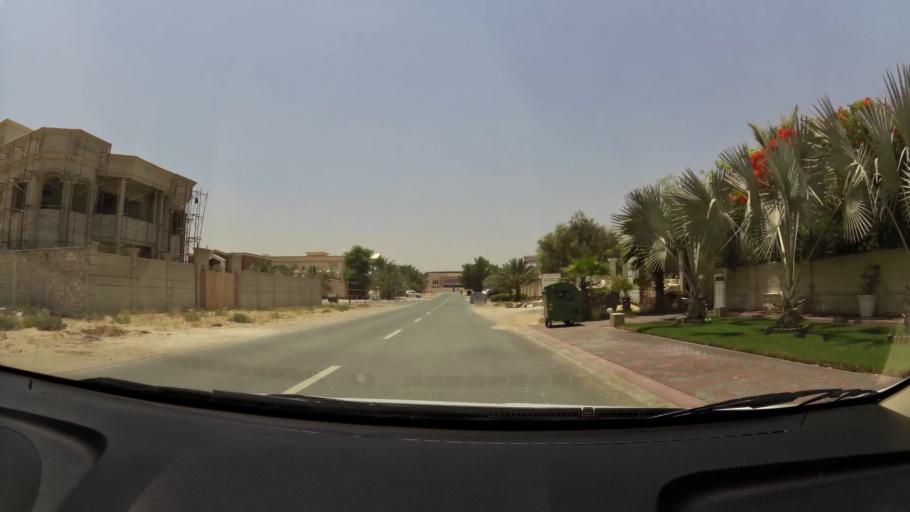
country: AE
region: Ajman
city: Ajman
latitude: 25.4063
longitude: 55.5016
